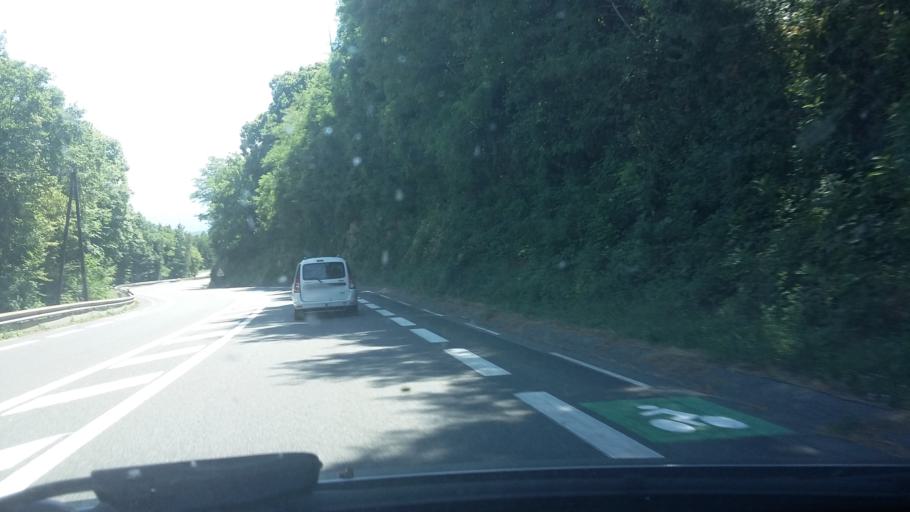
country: FR
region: Rhone-Alpes
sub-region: Departement de la Savoie
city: Le Bourget-du-Lac
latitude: 45.6727
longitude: 5.8540
